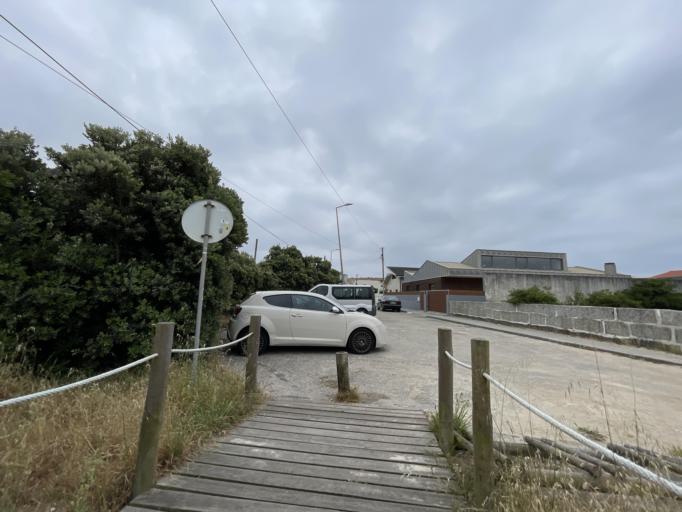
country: PT
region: Aveiro
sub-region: Ovar
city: Esmoriz
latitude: 40.9618
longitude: -8.6517
